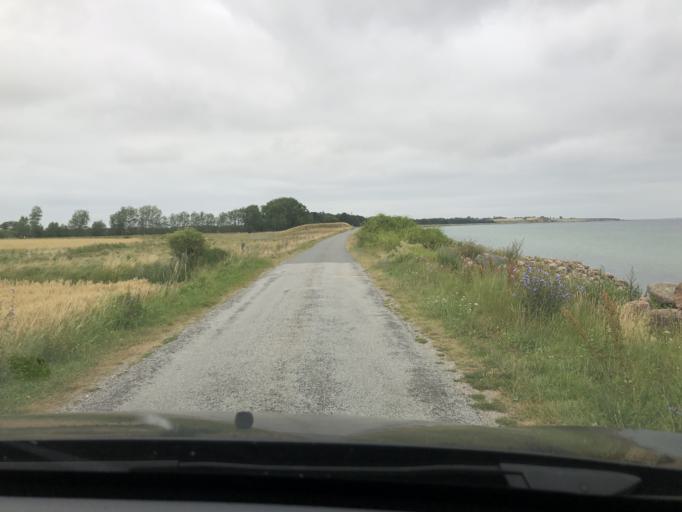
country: DK
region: South Denmark
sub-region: AEro Kommune
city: AEroskobing
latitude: 54.8346
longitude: 10.4439
